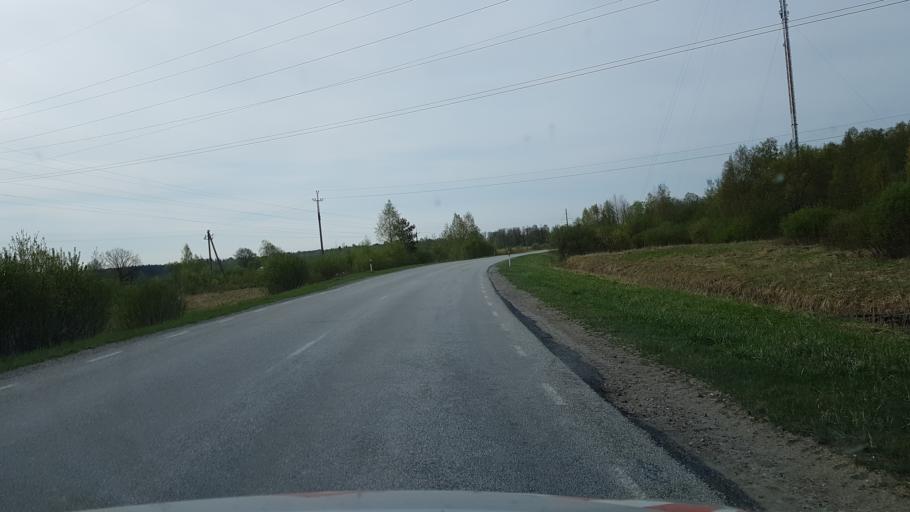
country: EE
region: Paernumaa
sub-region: Audru vald
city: Audru
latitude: 58.4185
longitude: 24.3112
